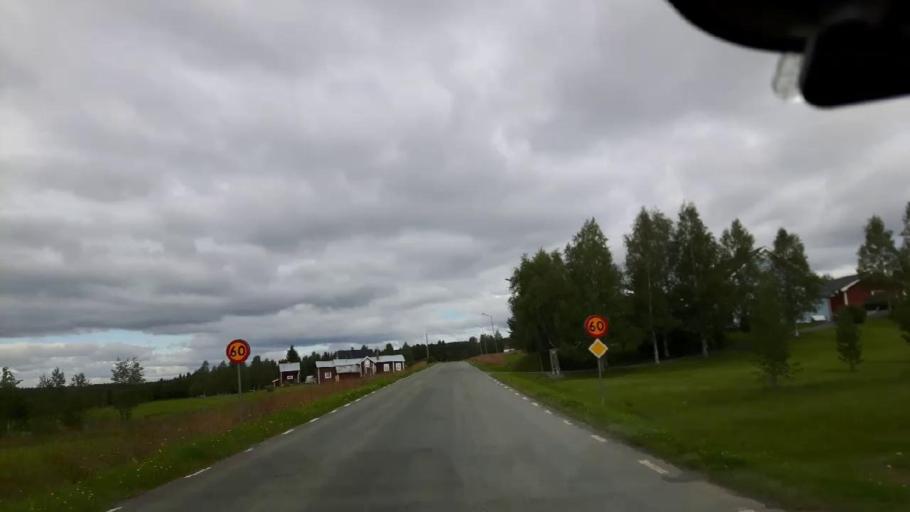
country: SE
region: Jaemtland
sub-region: Krokoms Kommun
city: Valla
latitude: 63.4971
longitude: 13.8976
